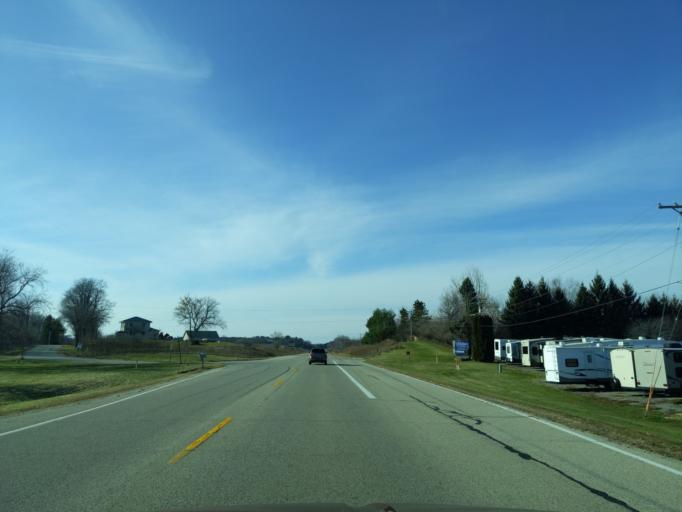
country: US
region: Wisconsin
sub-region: Rock County
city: Milton
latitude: 42.8252
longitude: -88.9867
